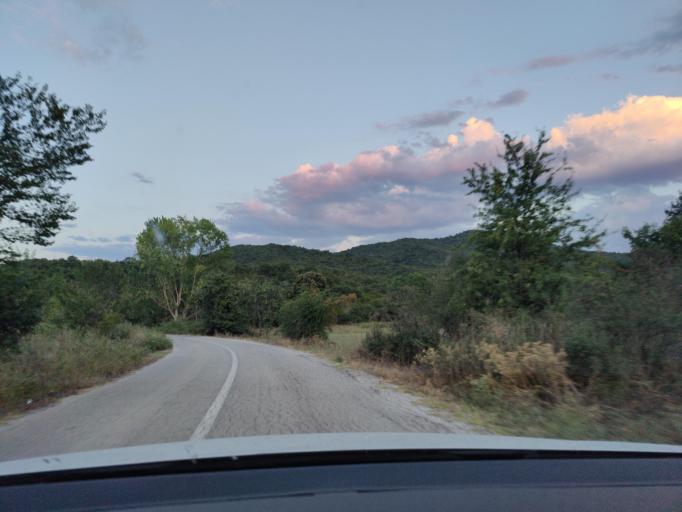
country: GR
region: Central Macedonia
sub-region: Nomos Serron
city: Chrysochorafa
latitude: 41.1793
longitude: 23.1419
